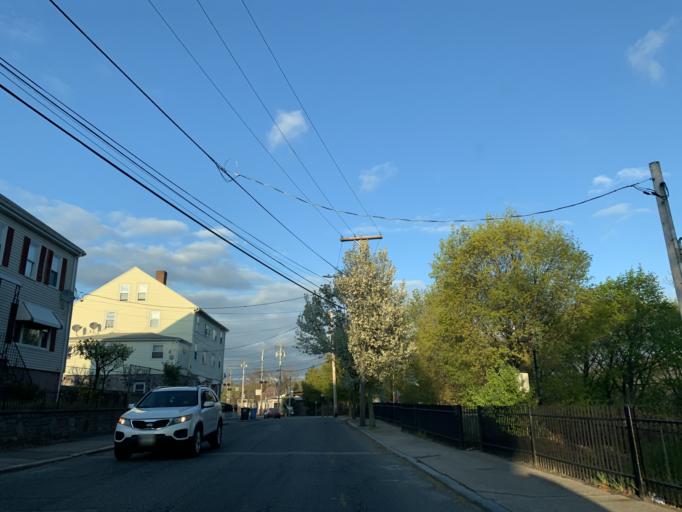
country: US
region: Rhode Island
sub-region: Providence County
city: Valley Falls
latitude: 41.9003
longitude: -71.3899
